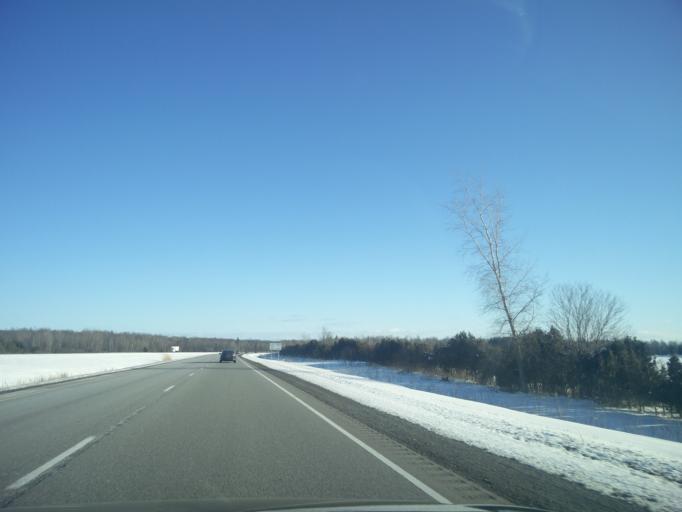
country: CA
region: Ontario
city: Prescott
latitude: 44.9425
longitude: -75.5805
